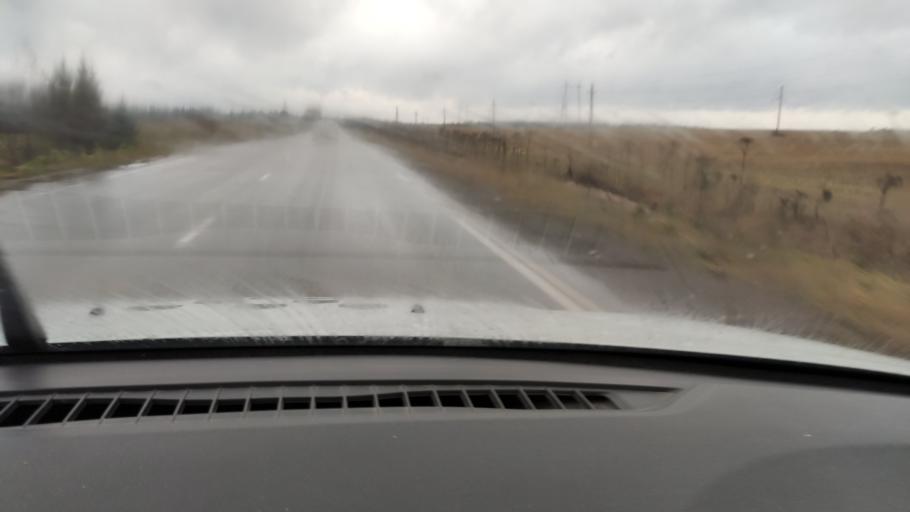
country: RU
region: Perm
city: Sylva
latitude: 58.0290
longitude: 56.7032
